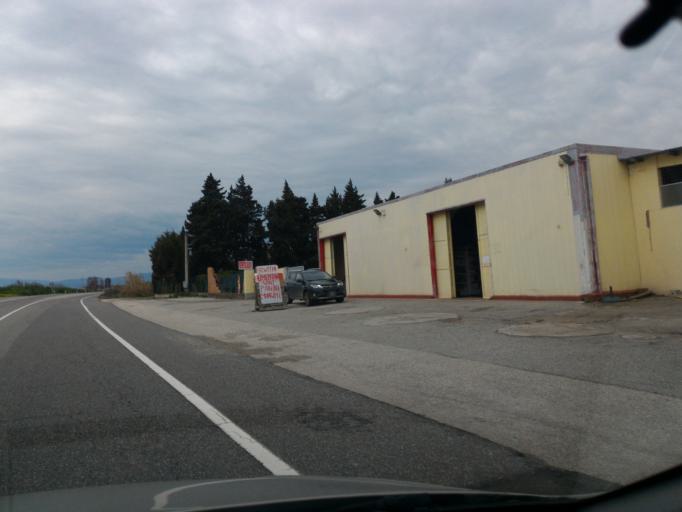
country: IT
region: Calabria
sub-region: Provincia di Catanzaro
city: Barone
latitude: 38.8551
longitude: 16.6710
